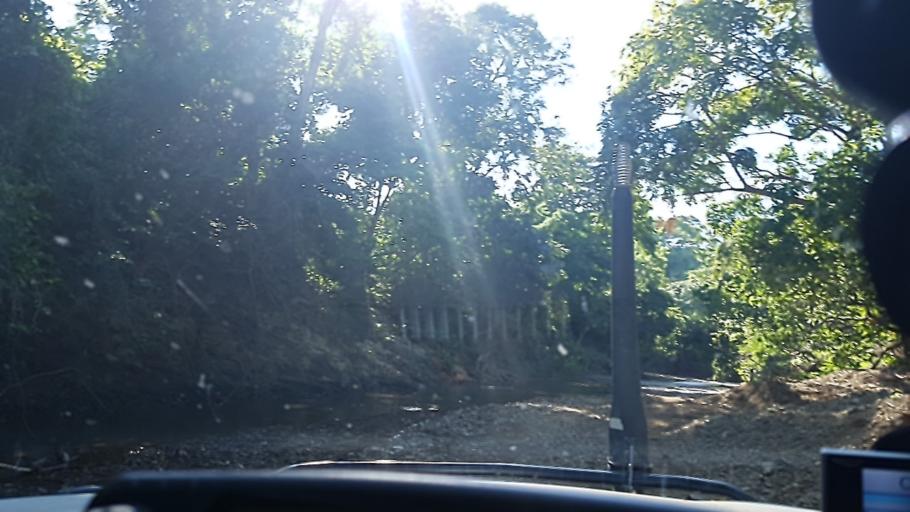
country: NI
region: Rivas
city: Tola
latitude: 11.5415
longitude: -86.1206
